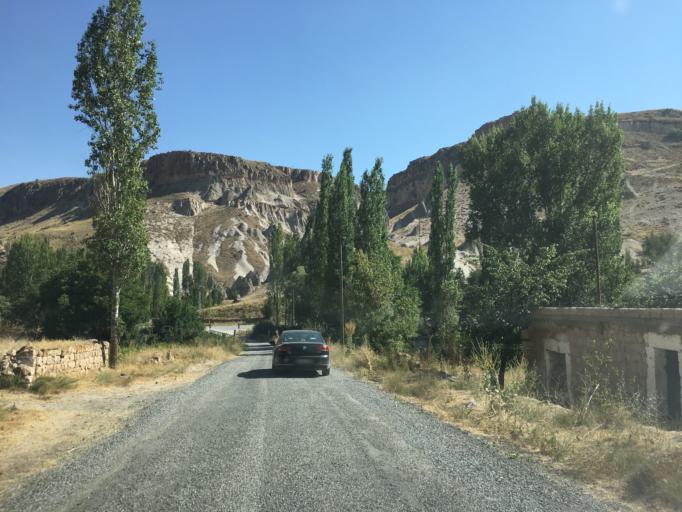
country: TR
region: Kayseri
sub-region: Yesilhisar
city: Yesilhisar
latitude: 38.3459
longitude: 34.9708
